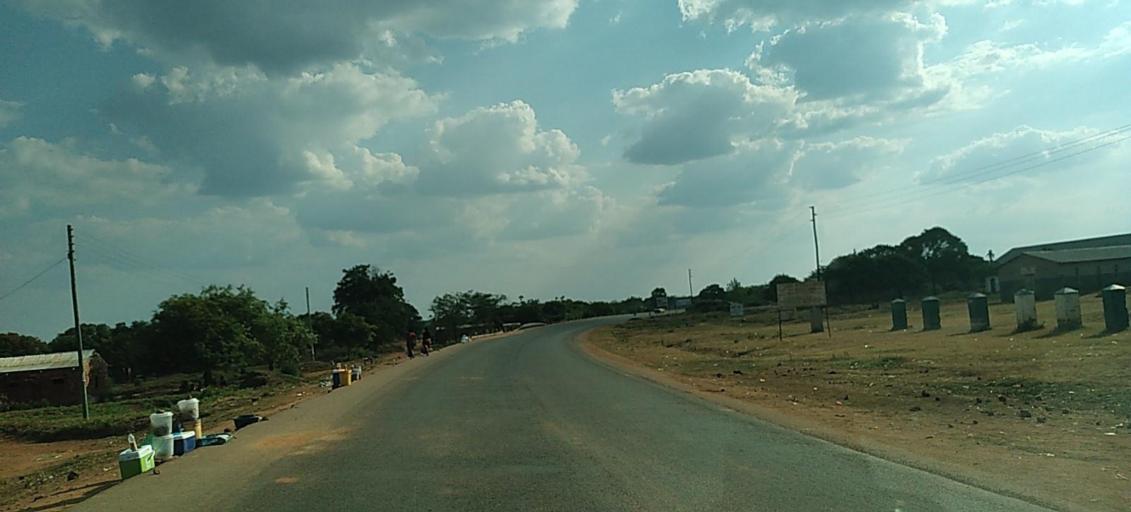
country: ZM
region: Copperbelt
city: Luanshya
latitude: -13.3604
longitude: 28.4138
